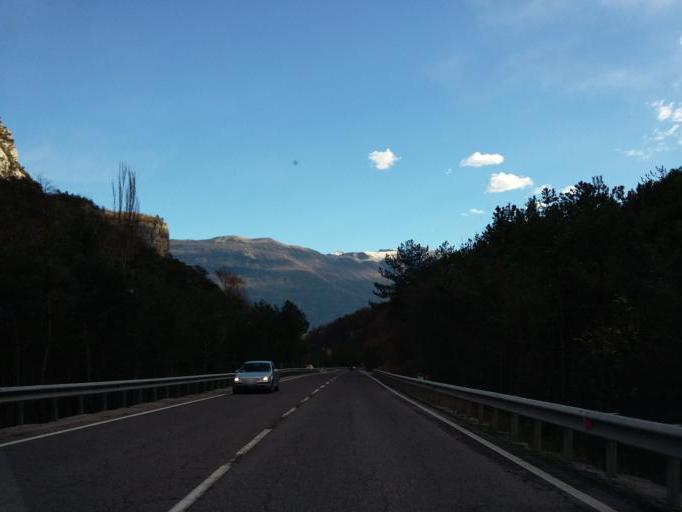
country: IT
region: Trentino-Alto Adige
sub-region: Provincia di Trento
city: Pietramurata
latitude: 46.0518
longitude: 10.9346
